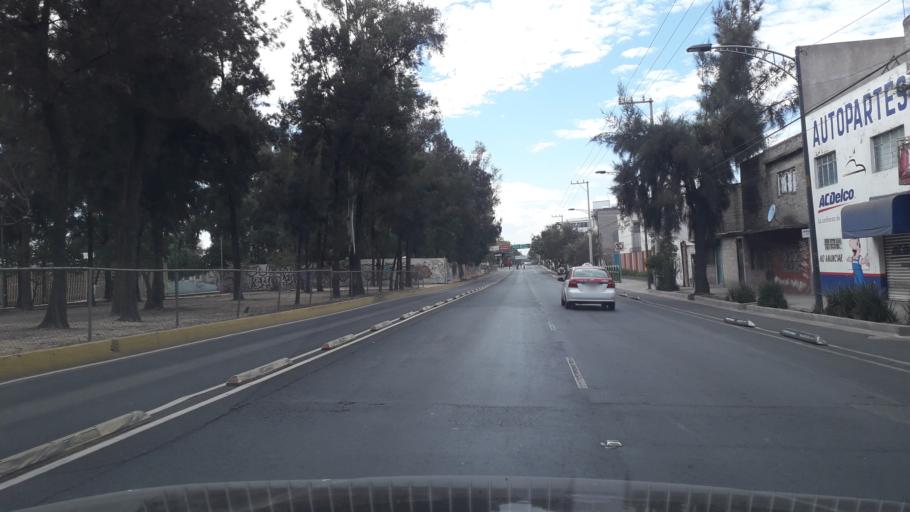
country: MX
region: Mexico City
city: Gustavo A. Madero
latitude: 19.4957
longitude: -99.0912
